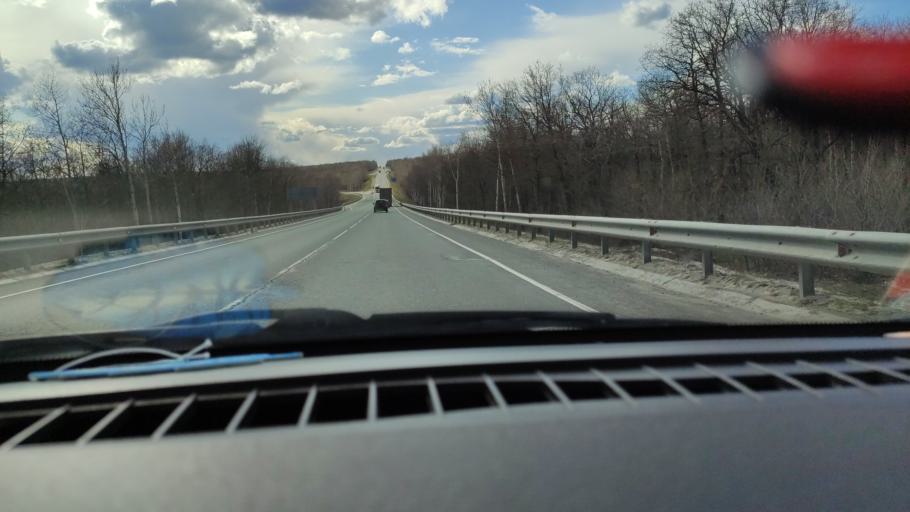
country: RU
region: Saratov
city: Vol'sk
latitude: 52.1087
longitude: 47.3824
